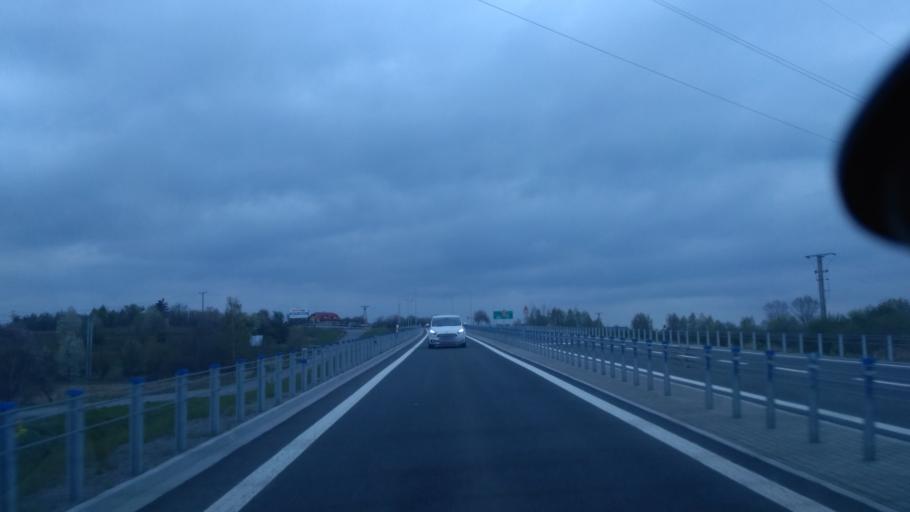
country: PL
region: Subcarpathian Voivodeship
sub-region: Powiat sanocki
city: Sanok
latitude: 49.5388
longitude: 22.2177
